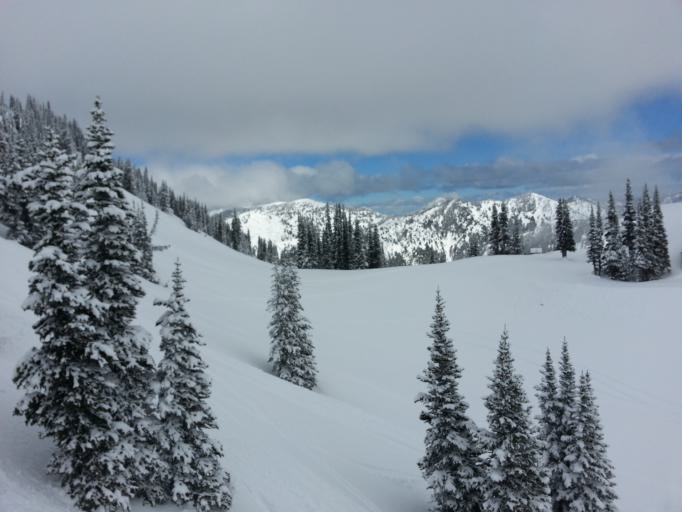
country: US
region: Washington
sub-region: King County
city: Enumclaw
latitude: 46.9253
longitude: -121.5034
